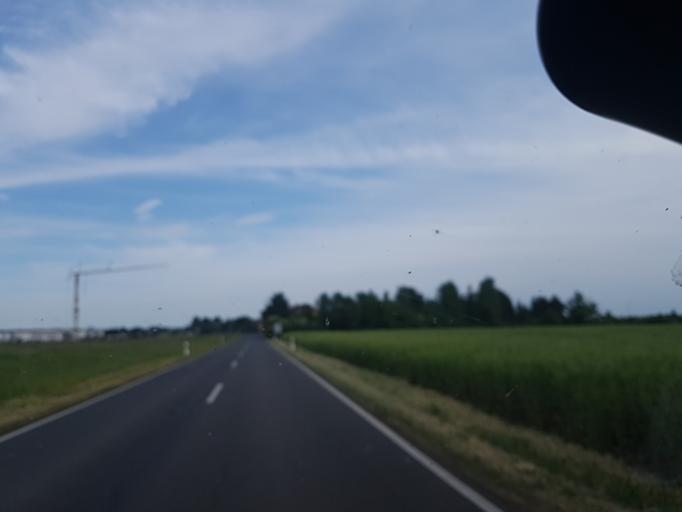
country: DE
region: Saxony-Anhalt
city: Zahna
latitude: 51.9277
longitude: 12.7772
